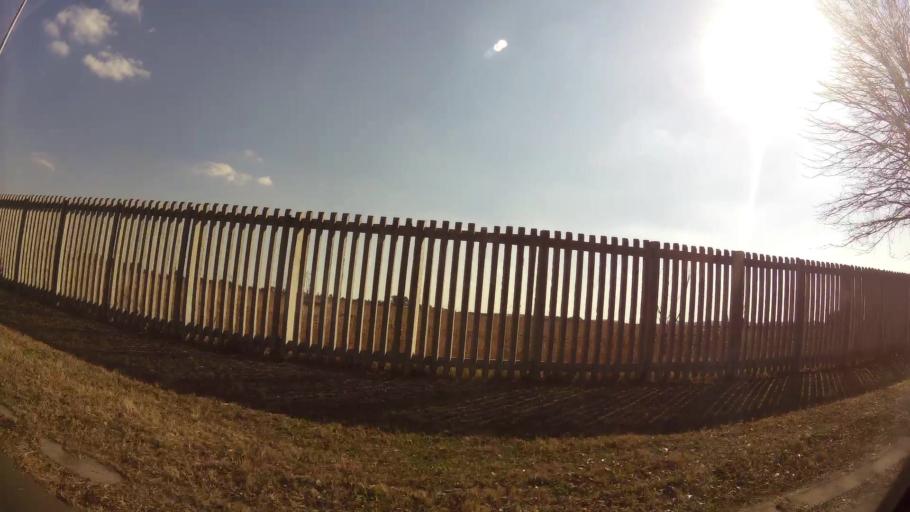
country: ZA
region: Gauteng
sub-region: Ekurhuleni Metropolitan Municipality
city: Boksburg
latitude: -26.2435
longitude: 28.3067
